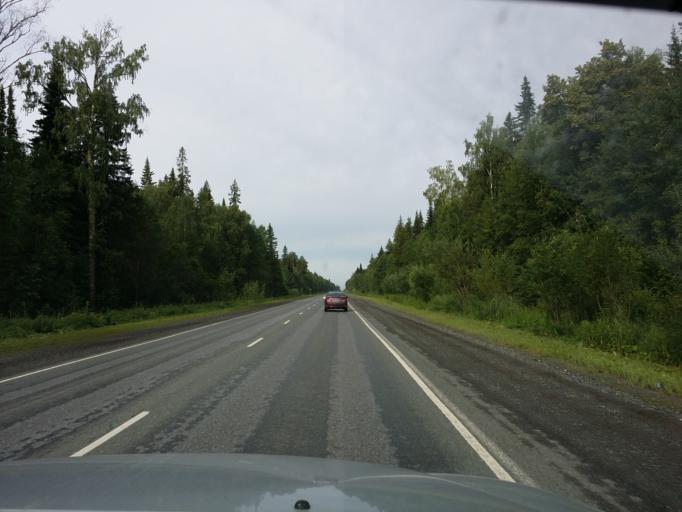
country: RU
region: Tjumen
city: Abalak
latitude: 58.4743
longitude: 68.5941
